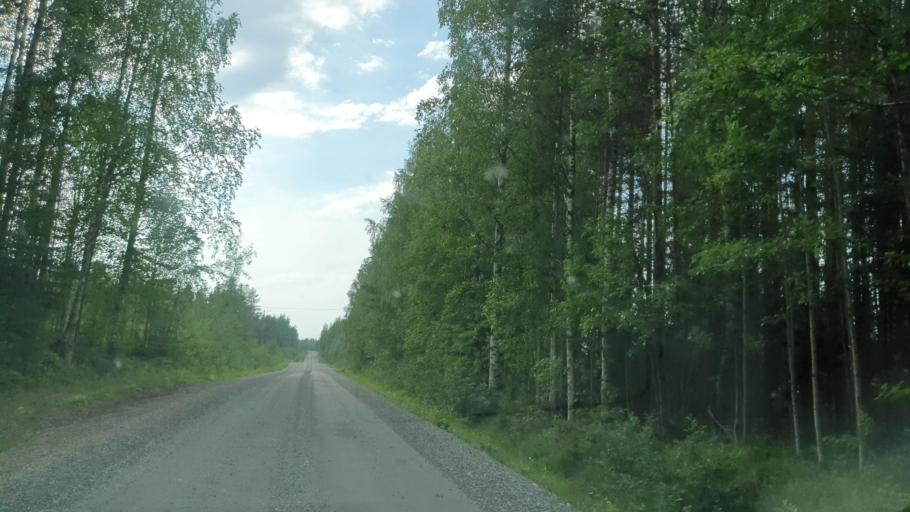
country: FI
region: Kainuu
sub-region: Kehys-Kainuu
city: Kuhmo
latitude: 64.0869
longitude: 29.6692
